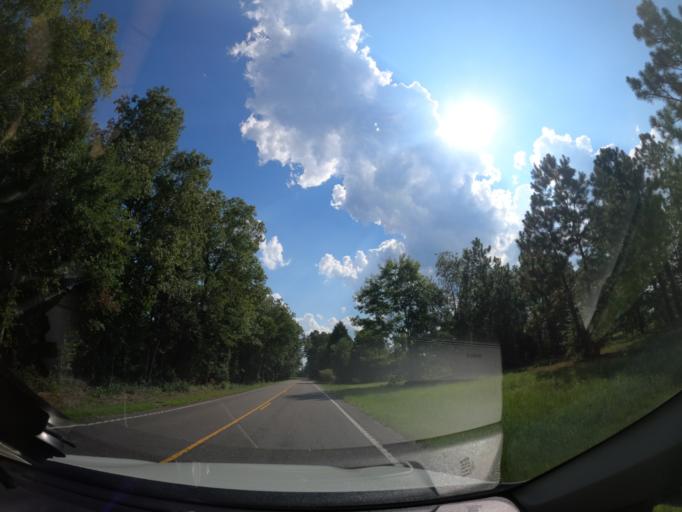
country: US
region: South Carolina
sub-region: Barnwell County
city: Williston
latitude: 33.5202
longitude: -81.5010
